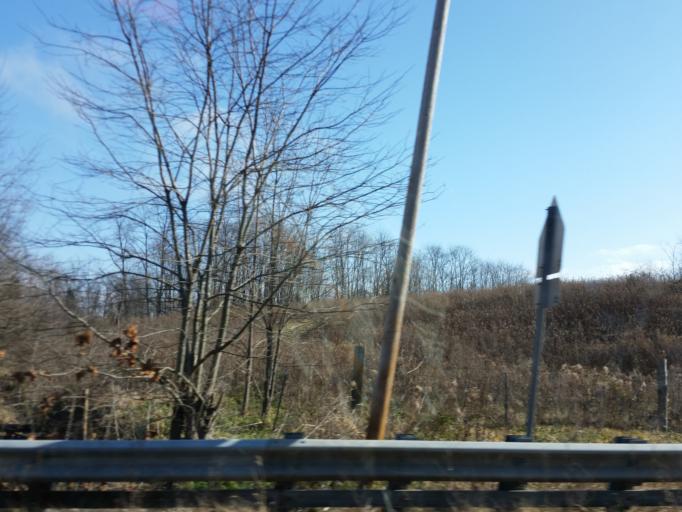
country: US
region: Indiana
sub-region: Jennings County
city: North Vernon
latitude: 38.8871
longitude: -85.5188
